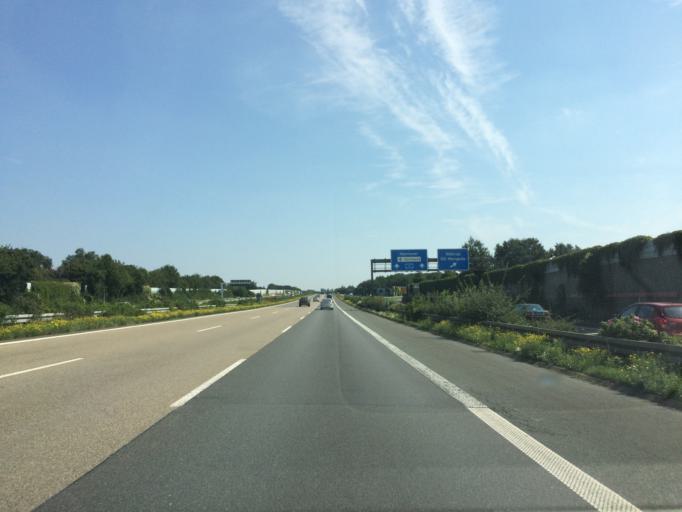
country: DE
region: North Rhine-Westphalia
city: Waltrop
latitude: 51.5843
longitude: 7.3855
